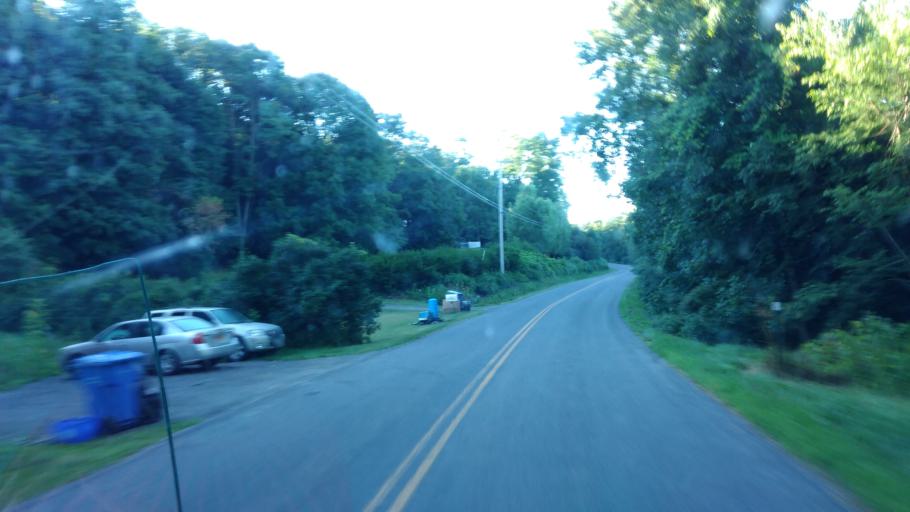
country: US
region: New York
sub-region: Wayne County
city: Lyons
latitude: 43.0832
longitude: -77.0182
